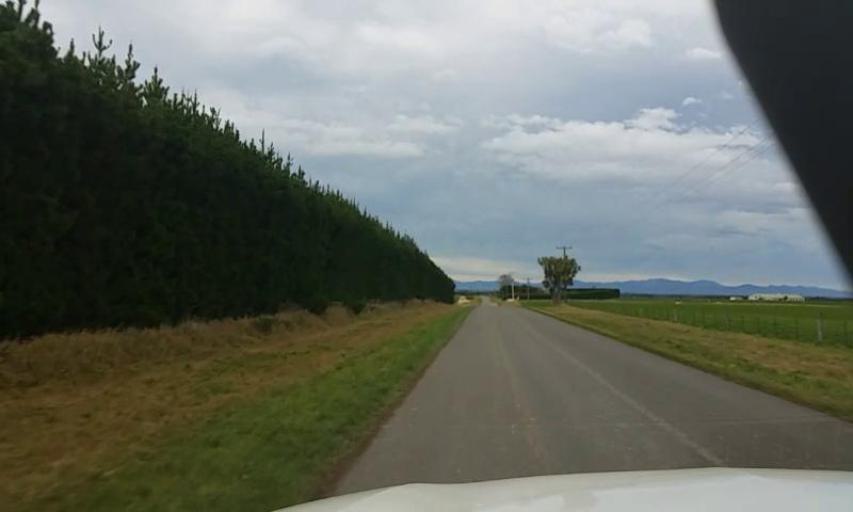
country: NZ
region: Canterbury
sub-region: Waimakariri District
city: Kaiapoi
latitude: -43.2932
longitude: 172.4725
